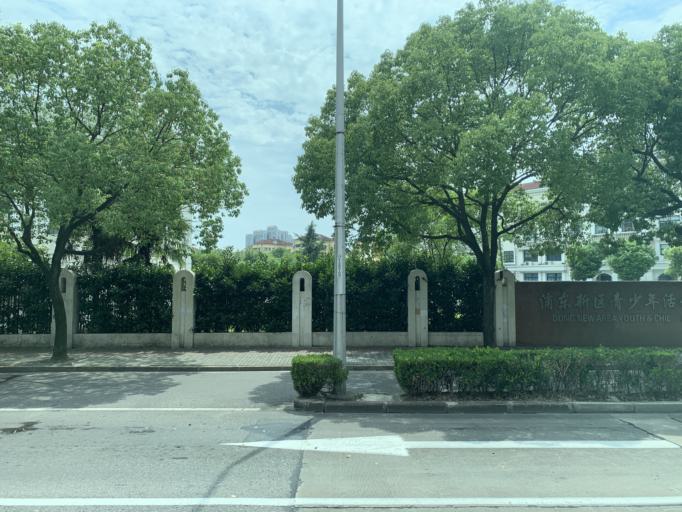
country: CN
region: Shanghai Shi
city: Huamu
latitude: 31.2506
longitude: 121.5791
